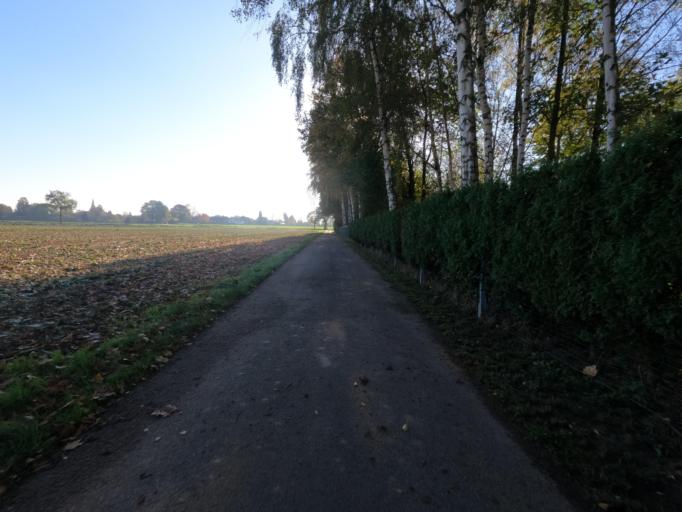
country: DE
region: North Rhine-Westphalia
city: Erkelenz
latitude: 51.0931
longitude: 6.3630
